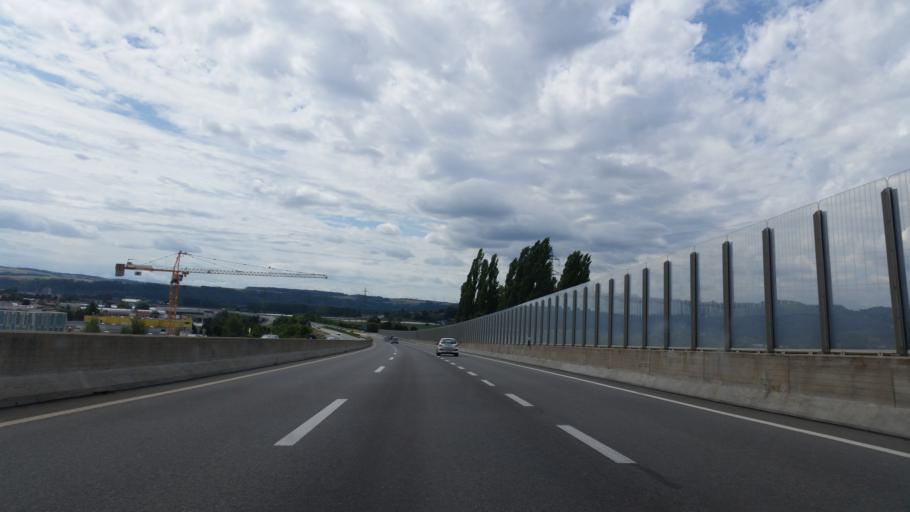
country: CH
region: Vaud
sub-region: Jura-Nord vaudois District
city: Montagny
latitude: 46.7947
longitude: 6.6196
